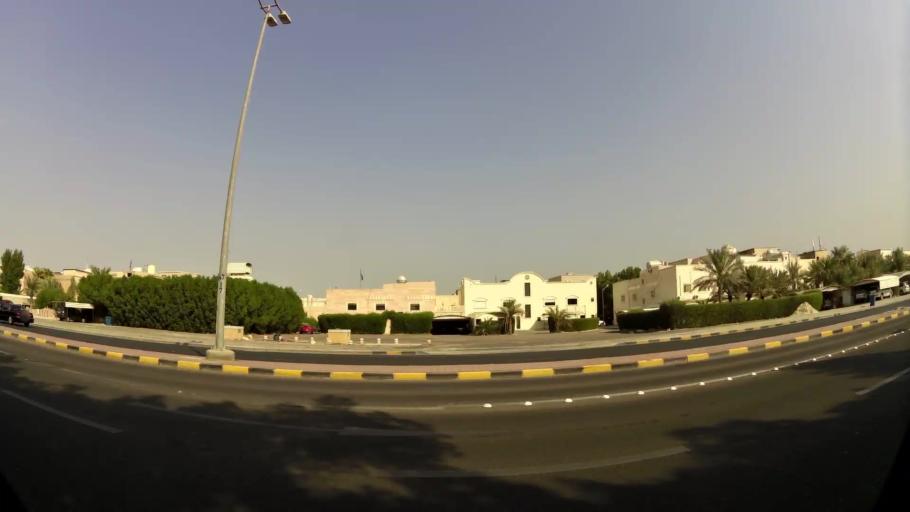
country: KW
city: Bayan
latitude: 29.2921
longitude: 48.0497
